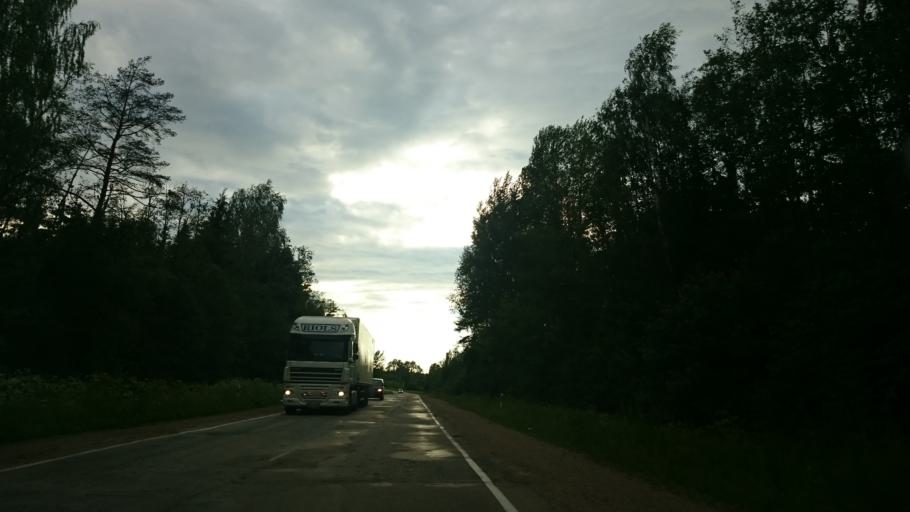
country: LV
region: Ludzas Rajons
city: Ludza
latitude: 56.5361
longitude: 27.6476
